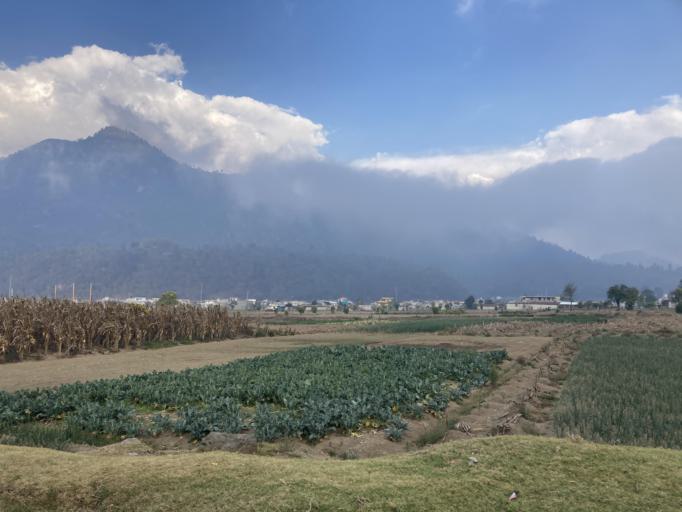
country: GT
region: Quetzaltenango
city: Almolonga
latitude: 14.7873
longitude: -91.5432
